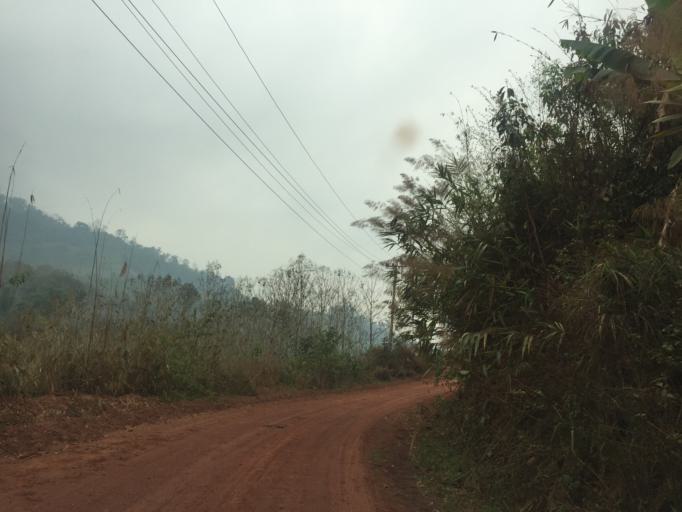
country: TH
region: Nan
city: Bo Kluea
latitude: 18.8631
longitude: 101.4345
